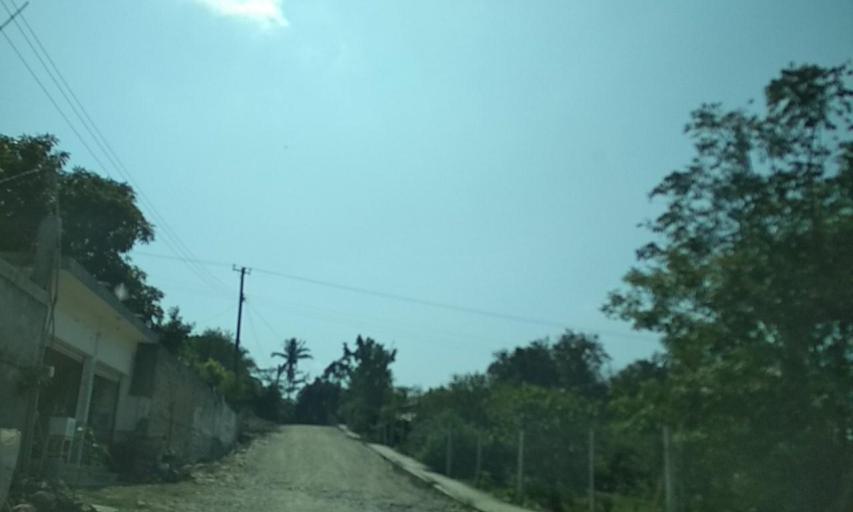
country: MX
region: Veracruz
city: Gutierrez Zamora
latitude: 20.3628
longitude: -97.1680
